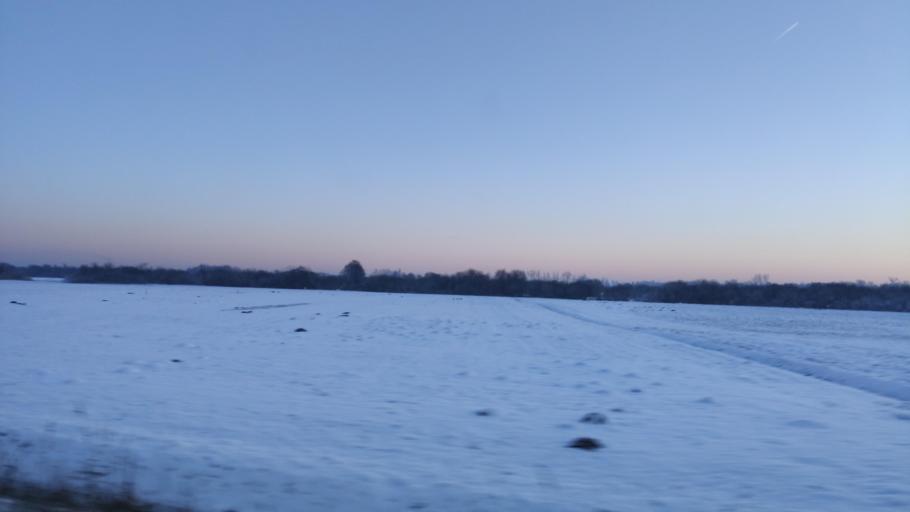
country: PL
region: Kujawsko-Pomorskie
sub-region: Powiat zninski
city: Barcin
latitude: 52.8763
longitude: 17.8693
